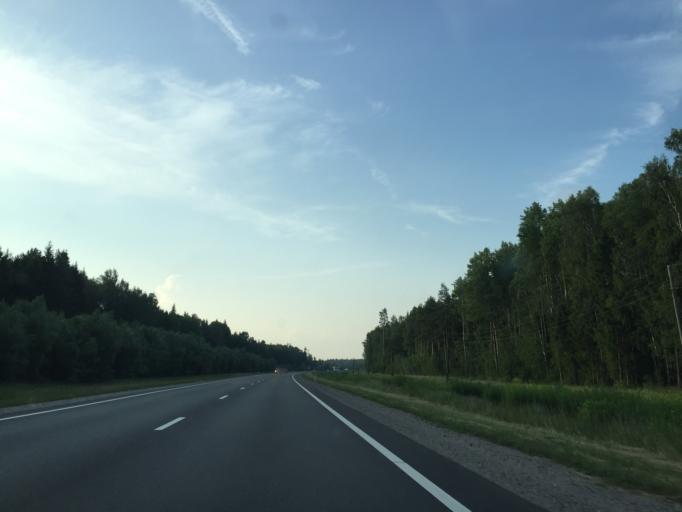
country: LV
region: Ozolnieku
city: Ozolnieki
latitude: 56.6807
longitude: 23.8218
